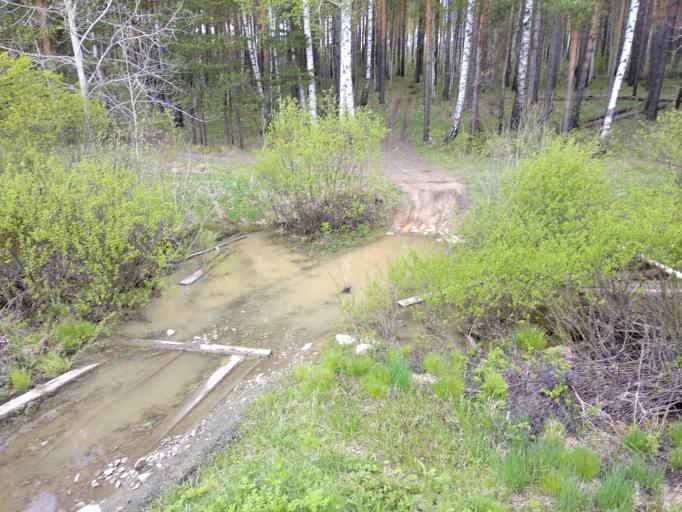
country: RU
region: Sverdlovsk
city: Beryozovsky
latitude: 56.9321
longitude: 60.7155
